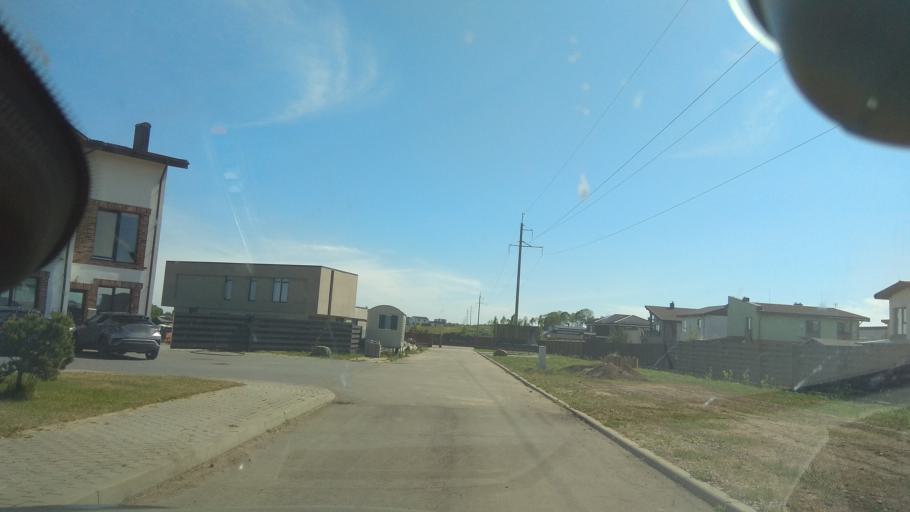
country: LT
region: Klaipedos apskritis
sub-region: Klaipeda
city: Klaipeda
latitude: 55.7487
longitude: 21.1826
